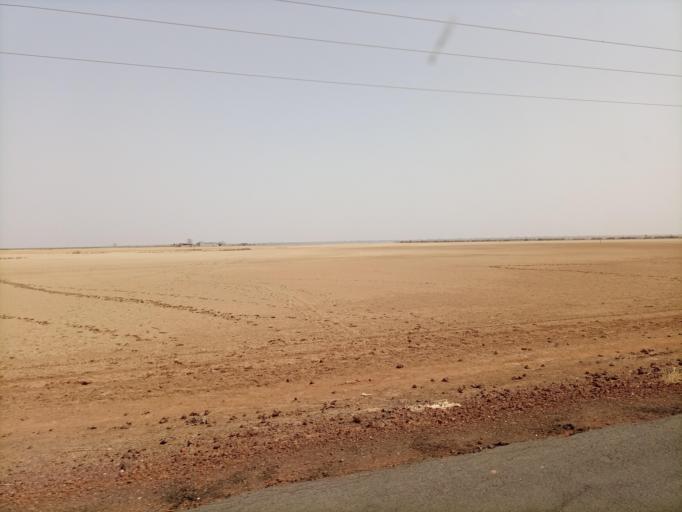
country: SN
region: Fatick
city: Foundiougne
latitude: 14.1693
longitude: -16.4620
